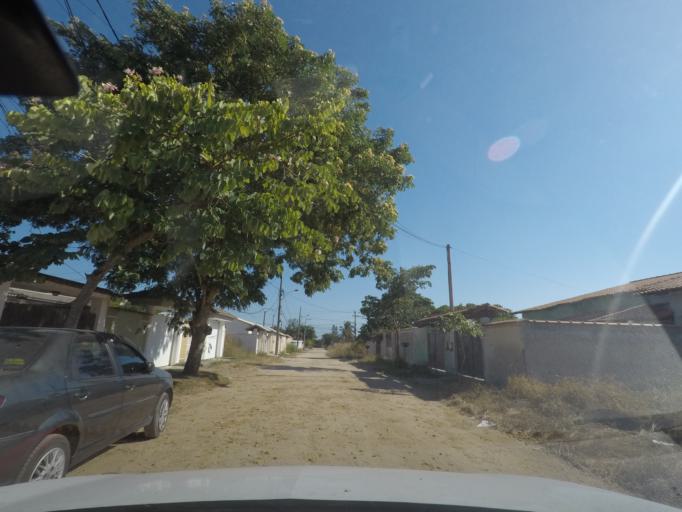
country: BR
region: Rio de Janeiro
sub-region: Marica
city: Marica
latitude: -22.9687
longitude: -42.9172
